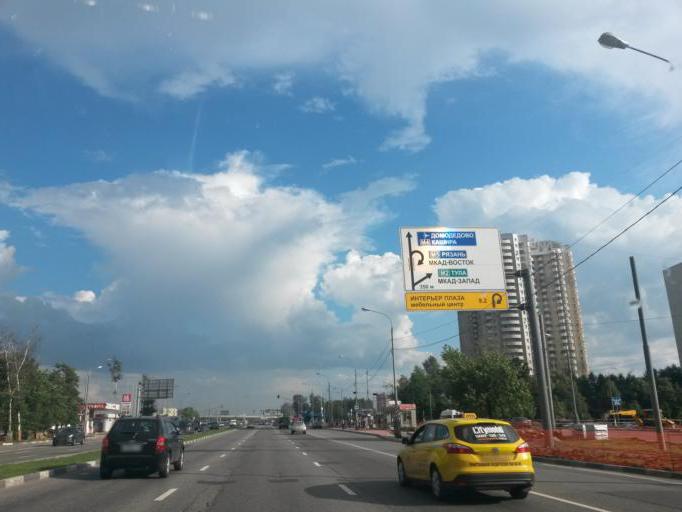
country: RU
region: Moscow
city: Orekhovo-Borisovo
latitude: 55.5978
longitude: 37.7247
